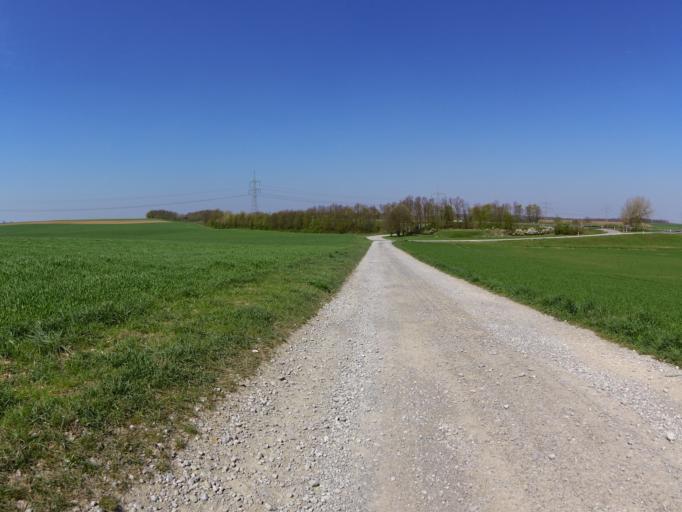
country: DE
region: Bavaria
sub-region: Regierungsbezirk Unterfranken
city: Biebelried
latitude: 49.7895
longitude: 10.0636
